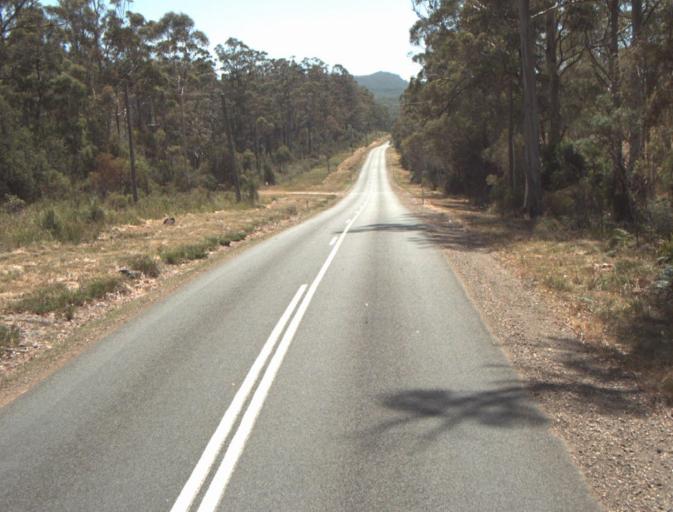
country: AU
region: Tasmania
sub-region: Launceston
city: Mayfield
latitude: -41.2932
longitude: 147.1310
